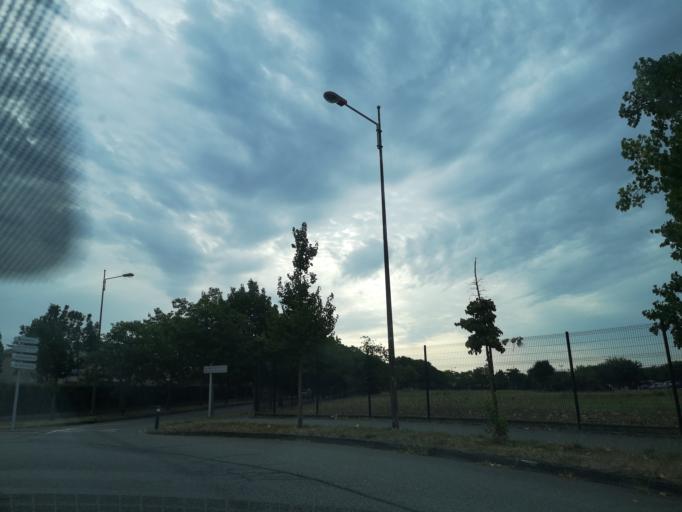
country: FR
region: Midi-Pyrenees
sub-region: Departement de la Haute-Garonne
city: Colomiers
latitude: 43.5809
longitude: 1.3748
